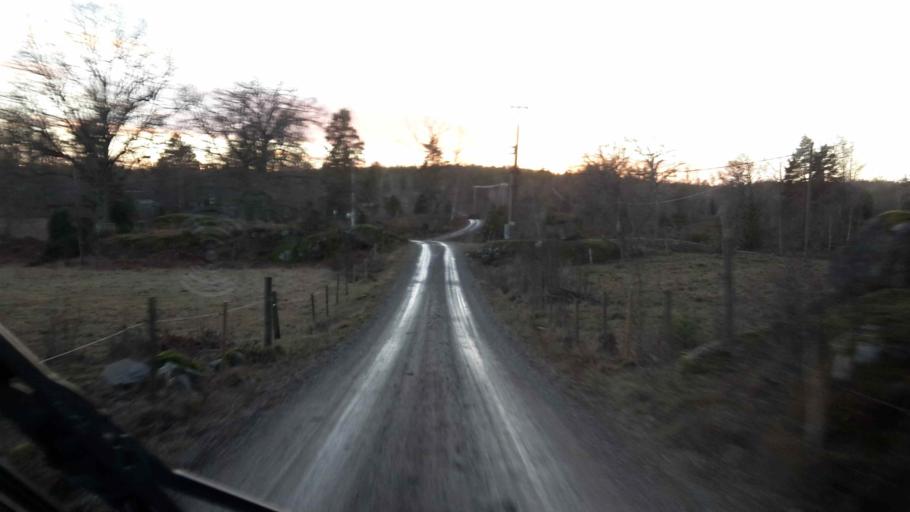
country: SE
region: OEstergoetland
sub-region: Atvidabergs Kommun
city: Atvidaberg
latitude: 58.2719
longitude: 16.0775
